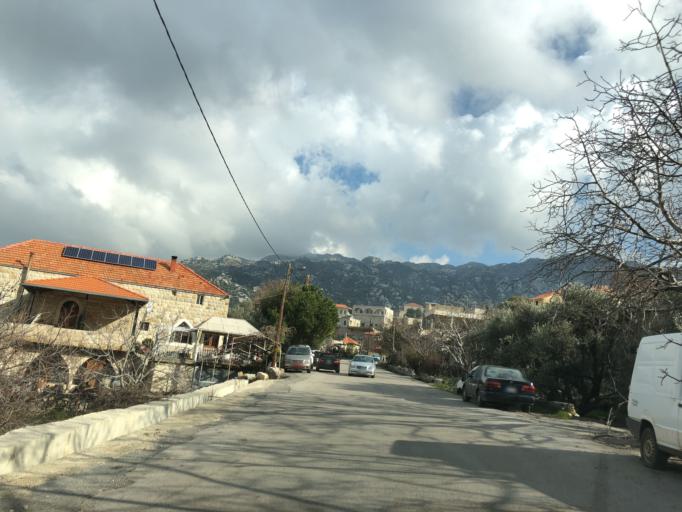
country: LB
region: Liban-Nord
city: Amioun
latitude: 34.2027
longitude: 35.8408
